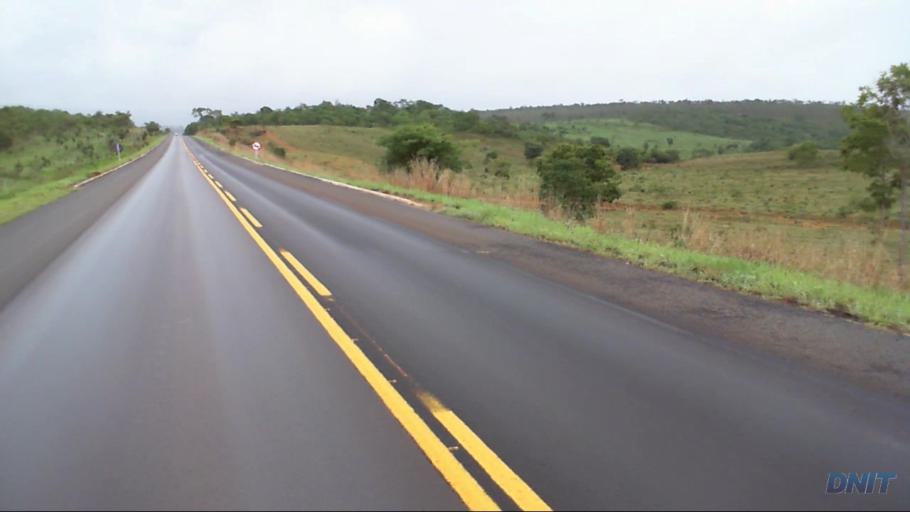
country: BR
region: Goias
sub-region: Padre Bernardo
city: Padre Bernardo
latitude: -15.2006
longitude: -48.4531
